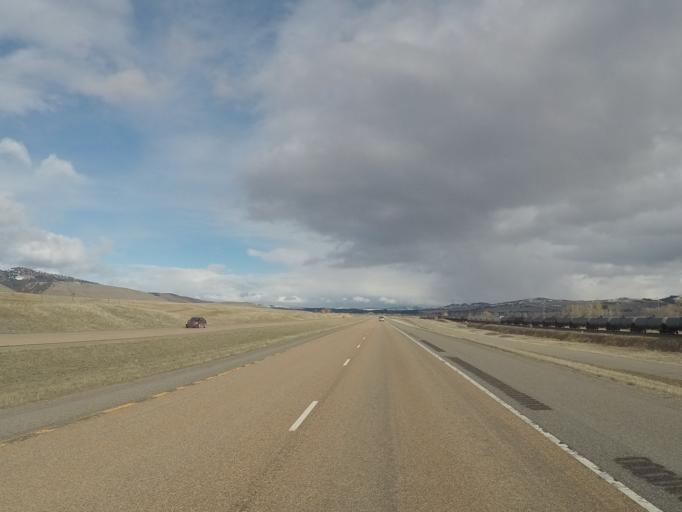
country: US
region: Montana
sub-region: Granite County
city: Philipsburg
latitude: 46.6191
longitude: -113.0578
